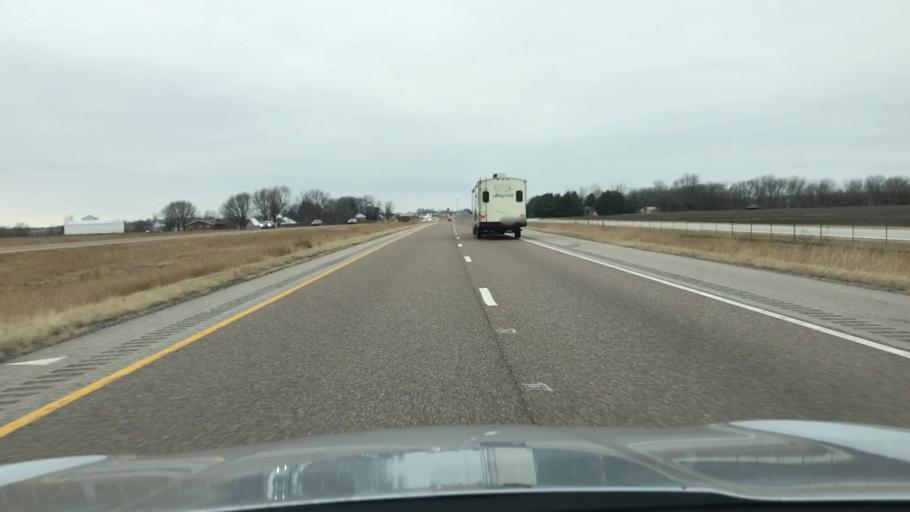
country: US
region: Illinois
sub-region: Madison County
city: Worden
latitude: 38.9419
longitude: -89.7877
